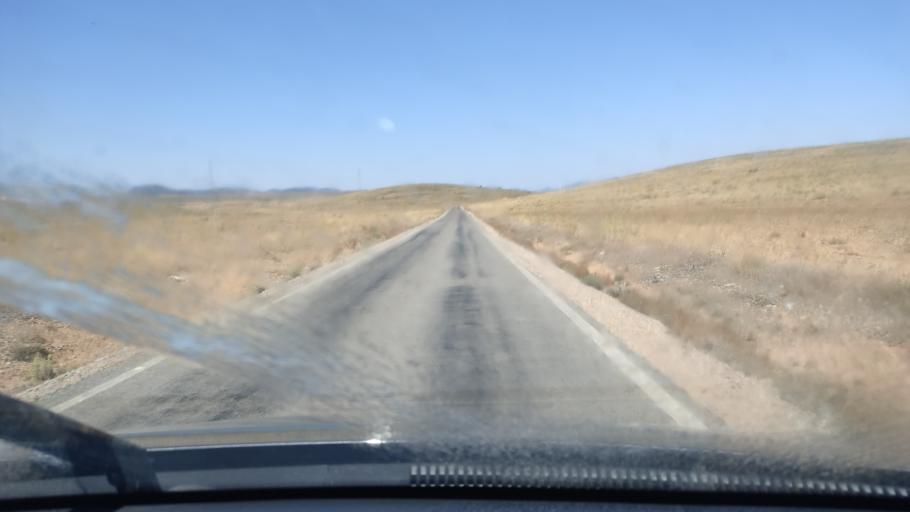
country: ES
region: Aragon
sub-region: Provincia de Teruel
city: Huesa del Comun
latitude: 41.0216
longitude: -0.9619
